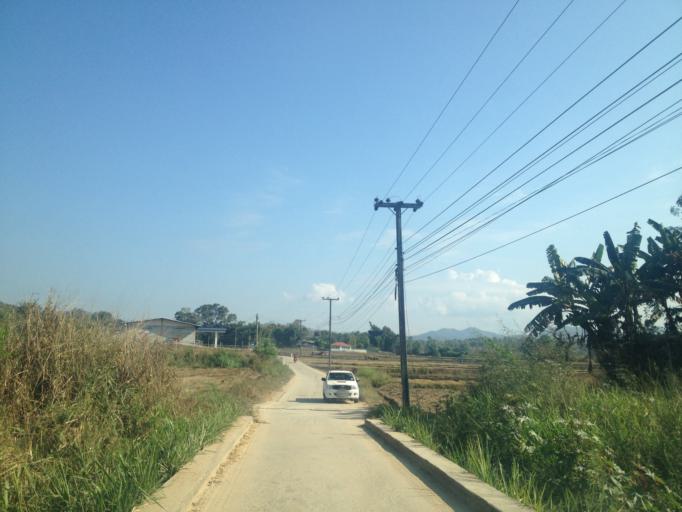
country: TH
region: Mae Hong Son
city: Ban Huai I Huak
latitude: 18.0903
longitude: 98.2026
